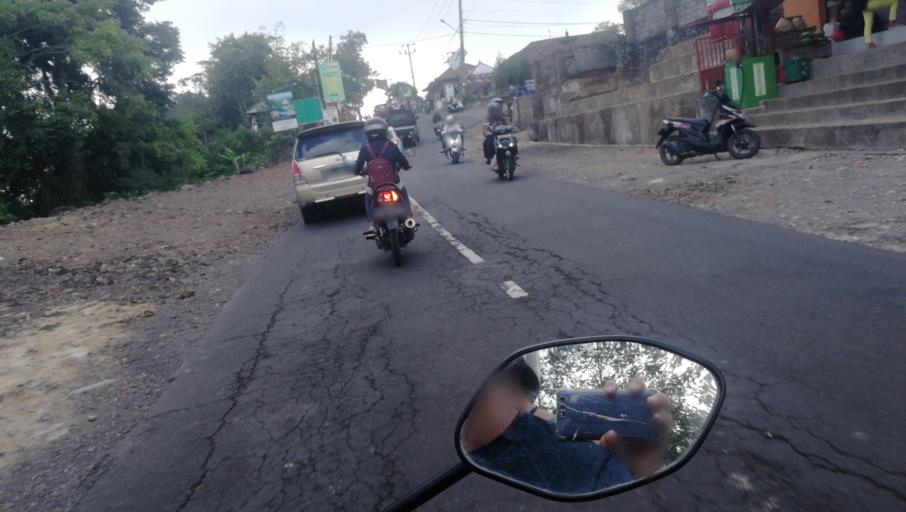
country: ID
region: Bali
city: Munduk
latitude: -8.2504
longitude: 115.0943
